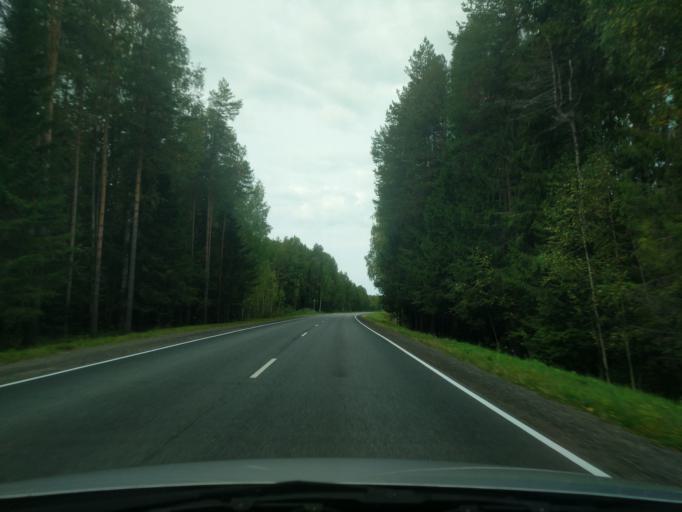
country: RU
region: Kirov
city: Svecha
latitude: 58.2706
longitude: 47.7196
